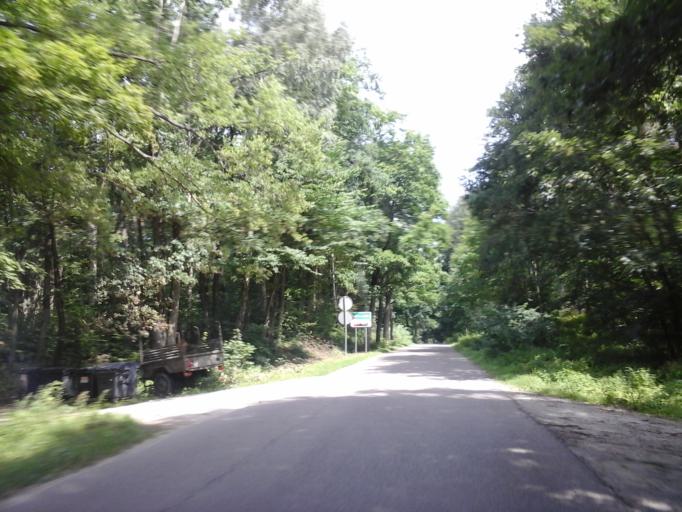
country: PL
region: West Pomeranian Voivodeship
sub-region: Powiat choszczenski
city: Bierzwnik
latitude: 53.0133
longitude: 15.6393
